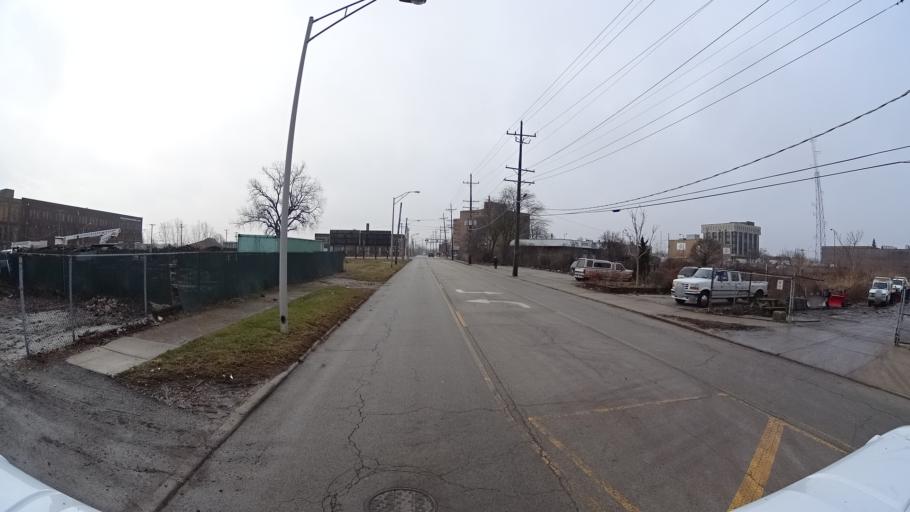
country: US
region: Illinois
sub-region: Cook County
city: Chicago Heights
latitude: 41.5024
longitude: -87.6339
